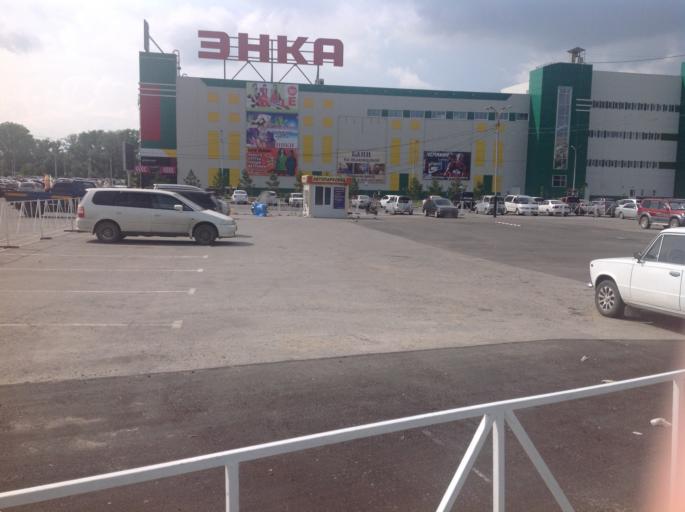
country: RU
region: Khabarovsk Krai
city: Khabarovsk Vtoroy
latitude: 48.3948
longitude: 135.1077
